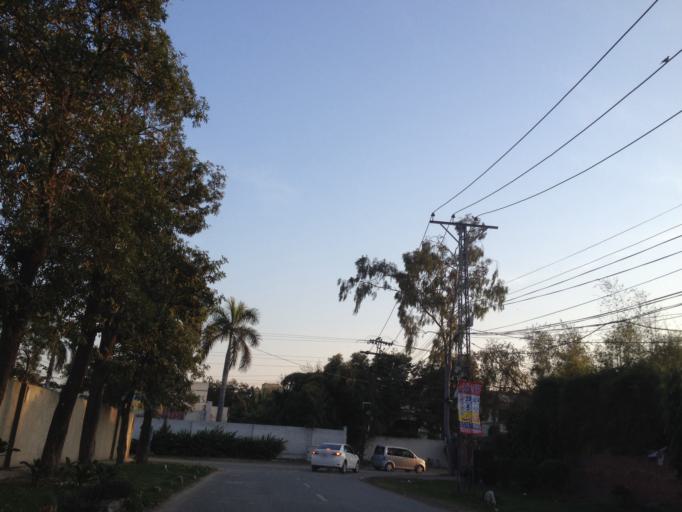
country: PK
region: Punjab
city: Lahore
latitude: 31.5000
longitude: 74.3283
